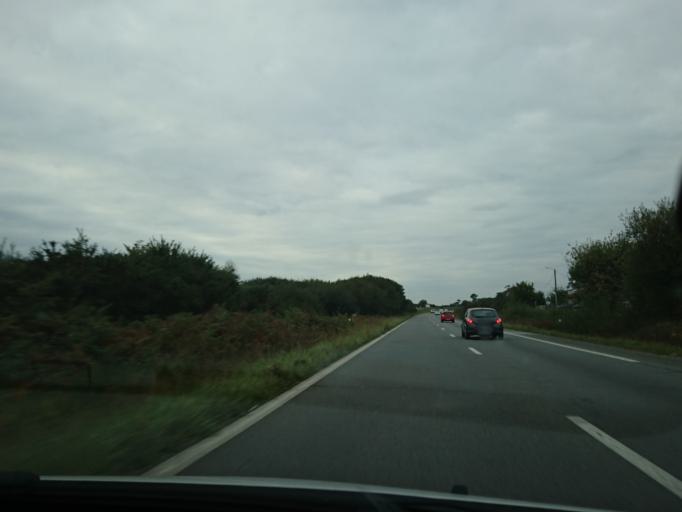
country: FR
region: Brittany
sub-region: Departement du Morbihan
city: Muzillac
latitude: 47.5653
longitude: -2.5109
